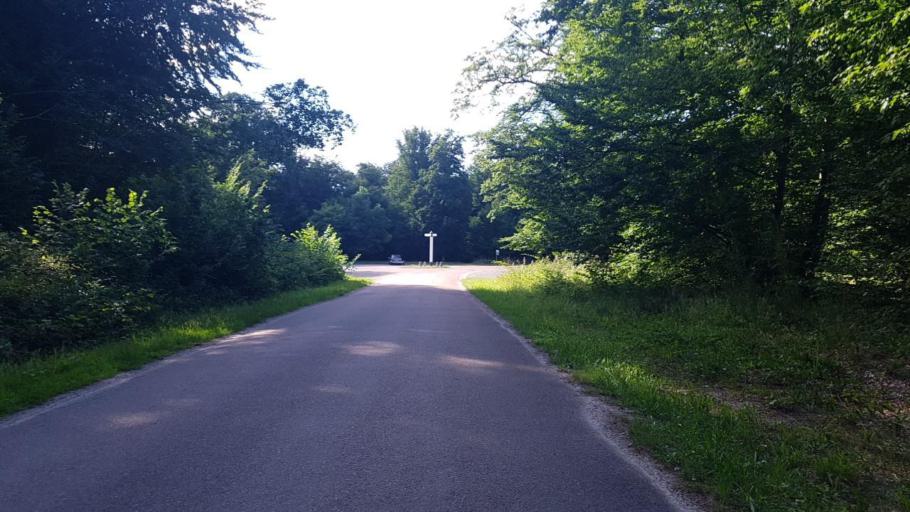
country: FR
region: Picardie
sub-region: Departement de l'Oise
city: Ver-sur-Launette
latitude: 49.1511
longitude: 2.6400
